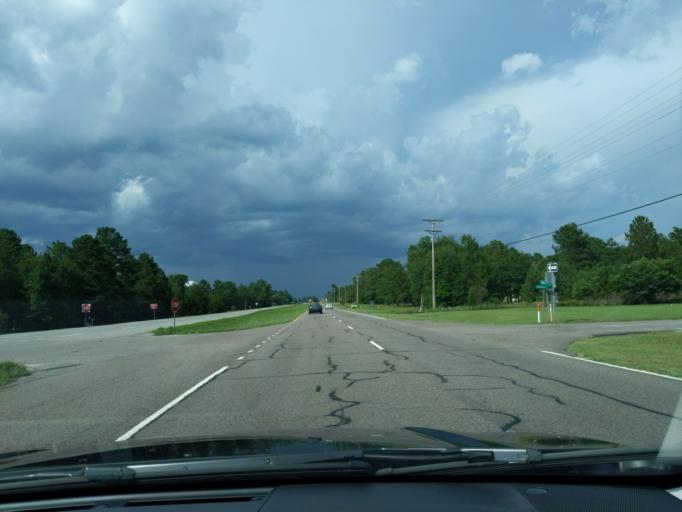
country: US
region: South Carolina
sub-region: Edgefield County
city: Murphys Estates
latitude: 33.6397
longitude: -81.9091
